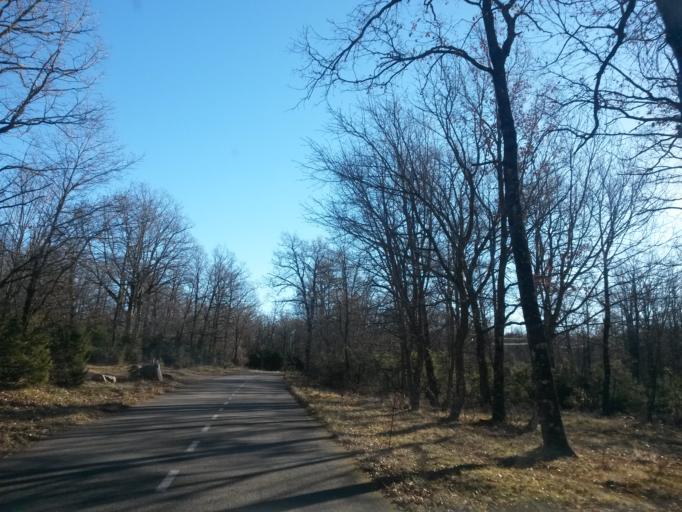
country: ES
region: Catalonia
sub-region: Provincia de Girona
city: les Planes d'Hostoles
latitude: 42.0292
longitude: 2.5293
